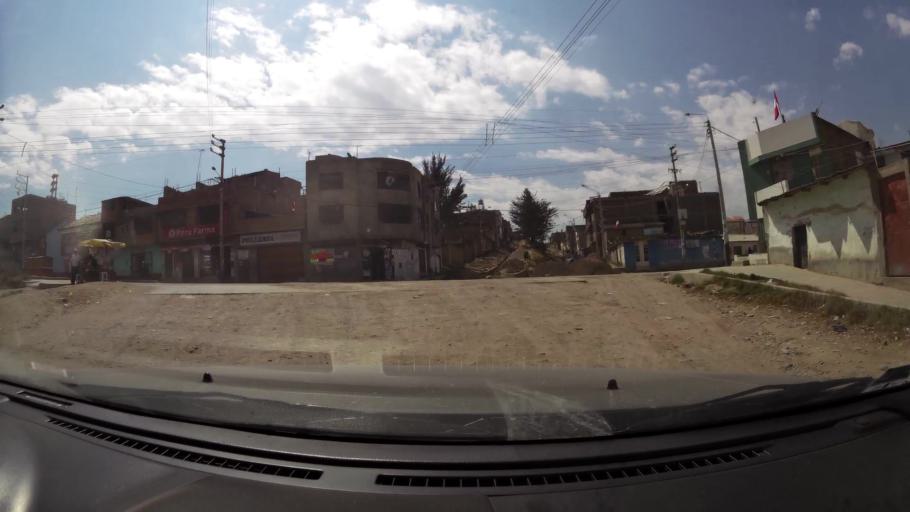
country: PE
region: Junin
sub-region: Provincia de Huancayo
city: Huancayo
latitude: -12.0731
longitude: -75.1969
